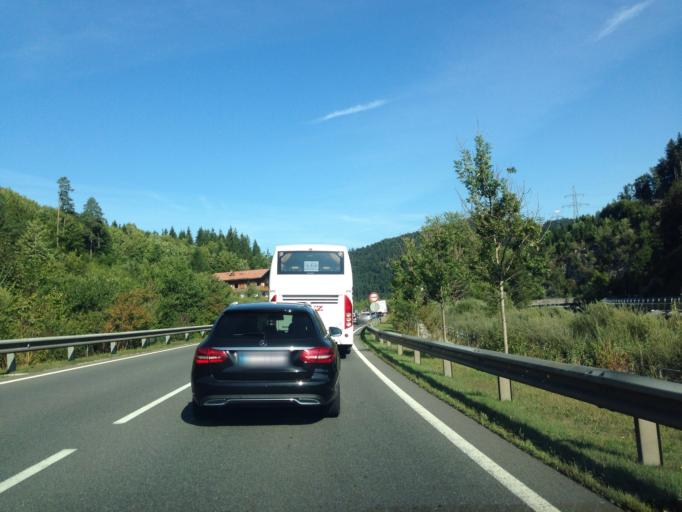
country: AT
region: Tyrol
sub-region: Politischer Bezirk Reutte
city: Musau
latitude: 47.5442
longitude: 10.6633
